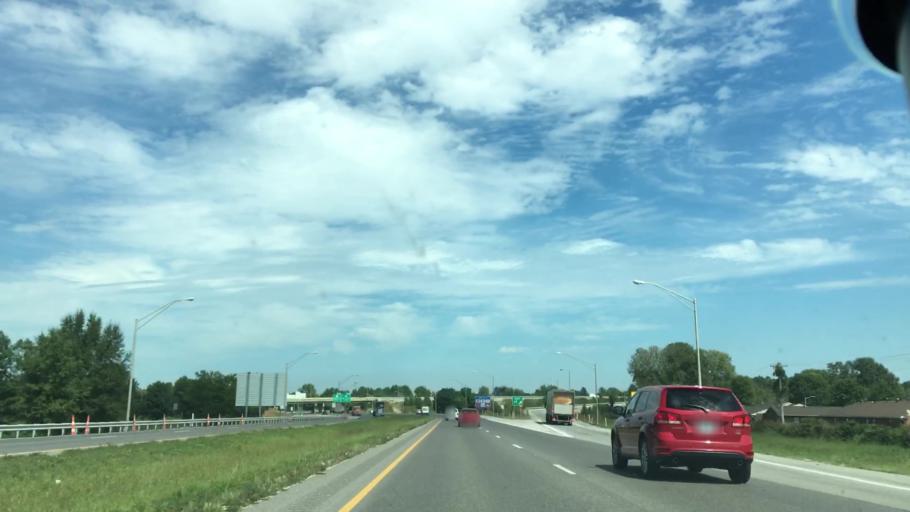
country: US
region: Kentucky
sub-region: Daviess County
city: Owensboro
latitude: 37.7378
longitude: -87.0770
